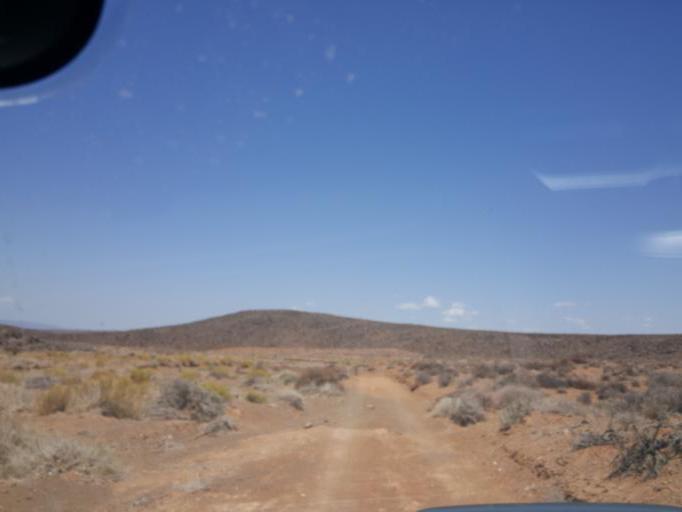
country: ZA
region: Northern Cape
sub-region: Namakwa District Municipality
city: Calvinia
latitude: -32.2075
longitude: 20.0131
